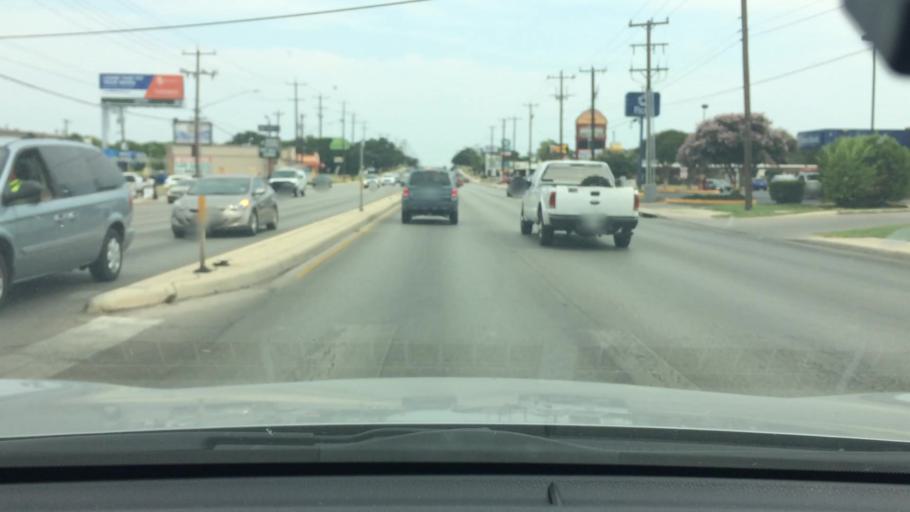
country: US
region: Texas
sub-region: Bexar County
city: Leon Valley
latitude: 29.4649
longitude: -98.6451
